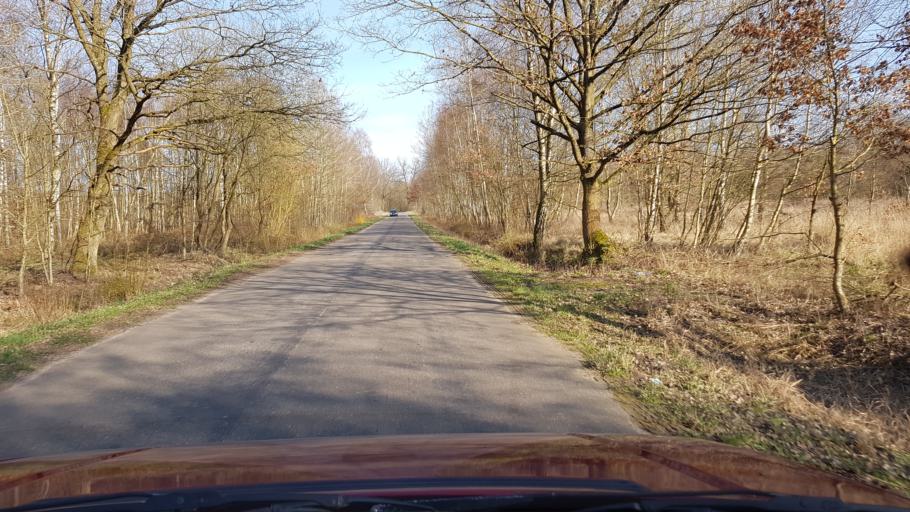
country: PL
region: West Pomeranian Voivodeship
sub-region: Powiat gryficki
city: Ploty
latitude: 53.8300
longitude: 15.3261
